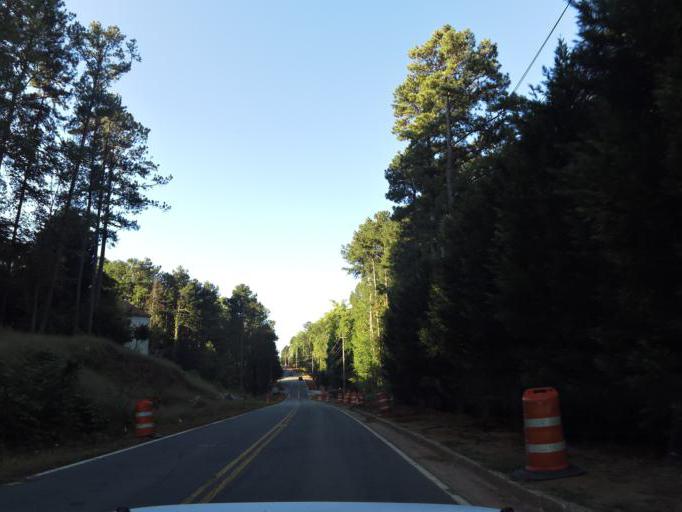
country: US
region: Georgia
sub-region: Cobb County
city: Kennesaw
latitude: 34.0031
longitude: -84.6399
